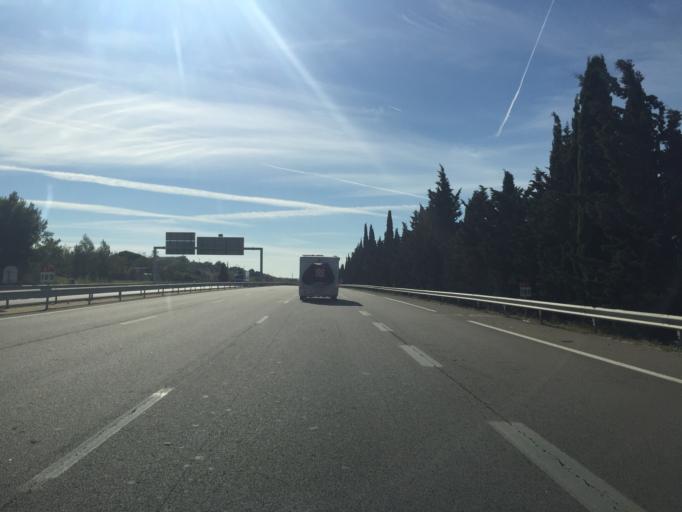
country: FR
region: Provence-Alpes-Cote d'Azur
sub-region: Departement du Vaucluse
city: Vedene
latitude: 43.9764
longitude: 4.8943
